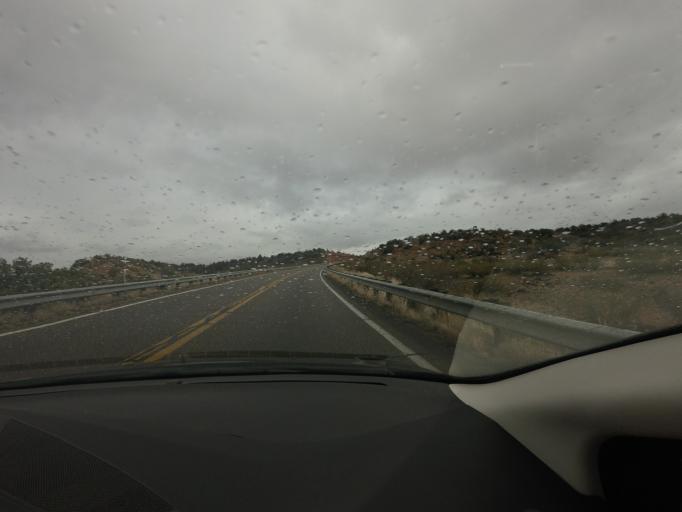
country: US
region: Arizona
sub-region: Yavapai County
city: Cornville
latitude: 34.6996
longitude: -111.8619
